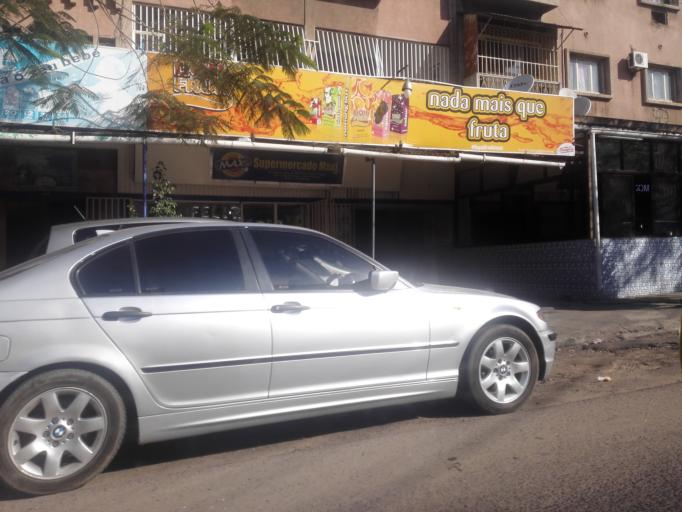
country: MZ
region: Maputo City
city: Maputo
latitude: -25.9621
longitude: 32.5821
